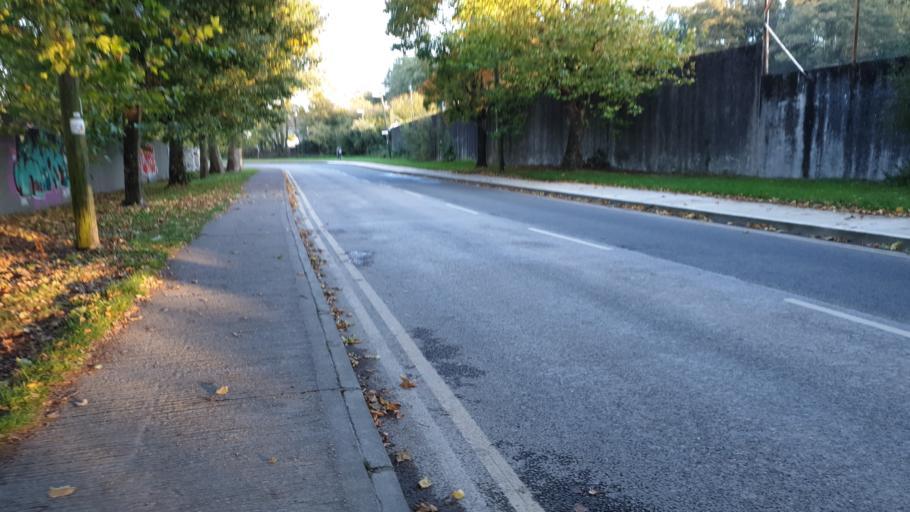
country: IE
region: Munster
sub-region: County Cork
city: Cork
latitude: 51.8978
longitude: -8.4404
